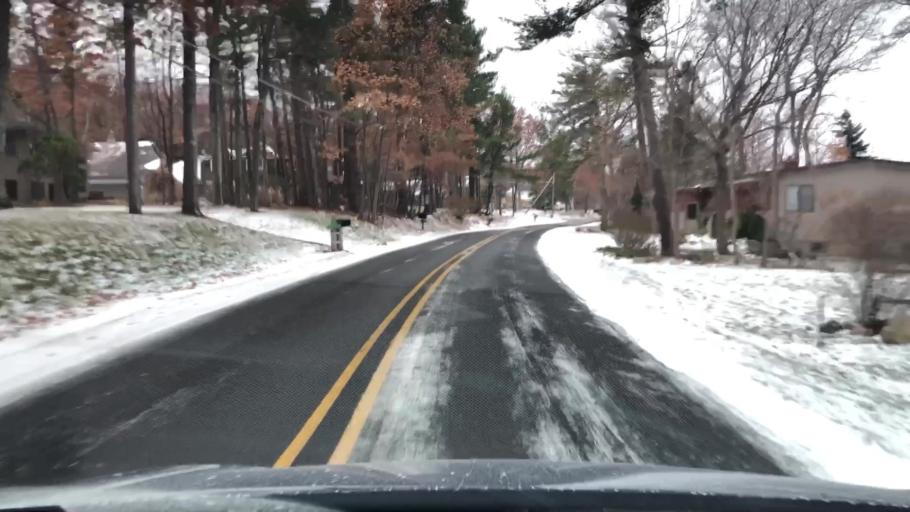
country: US
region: Michigan
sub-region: Grand Traverse County
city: Traverse City
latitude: 44.8223
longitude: -85.5716
